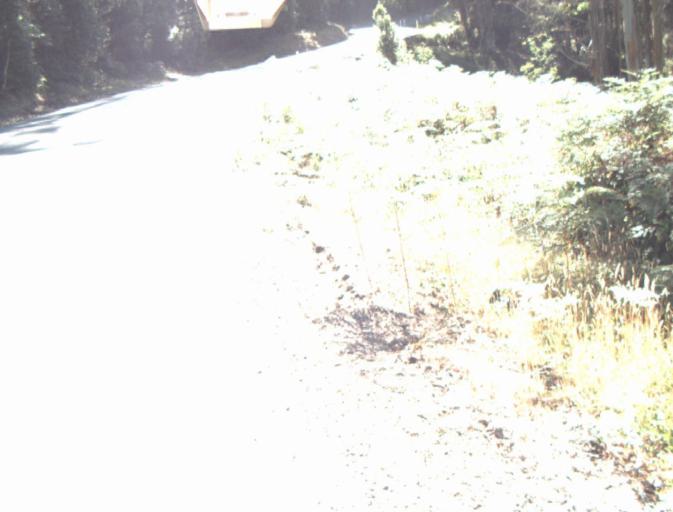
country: AU
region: Tasmania
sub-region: Dorset
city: Scottsdale
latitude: -41.2683
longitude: 147.3768
